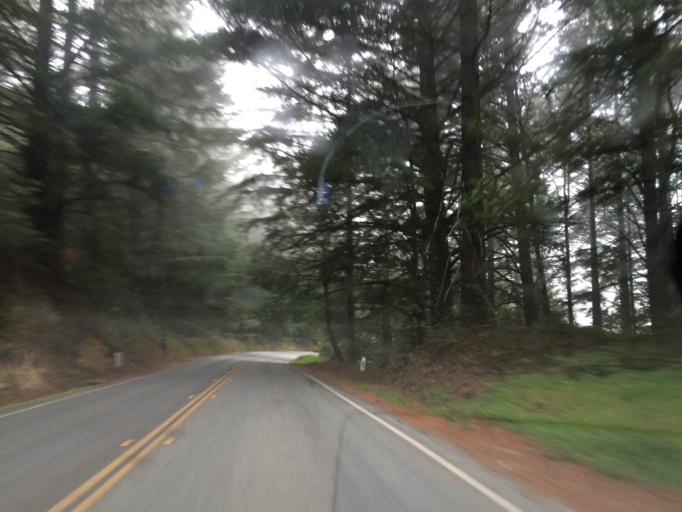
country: US
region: California
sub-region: Santa Clara County
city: Loyola
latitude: 37.2462
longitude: -122.1470
